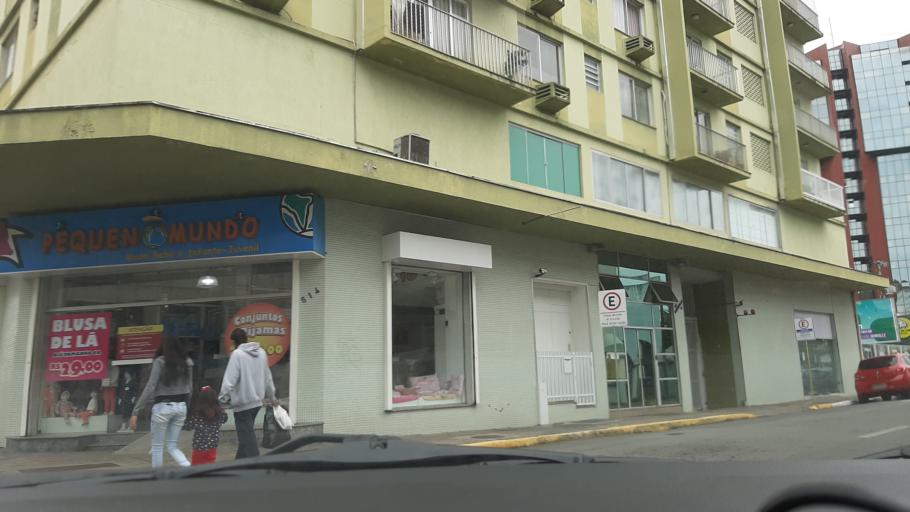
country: BR
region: Santa Catarina
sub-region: Joinville
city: Joinville
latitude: -26.3036
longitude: -48.8458
